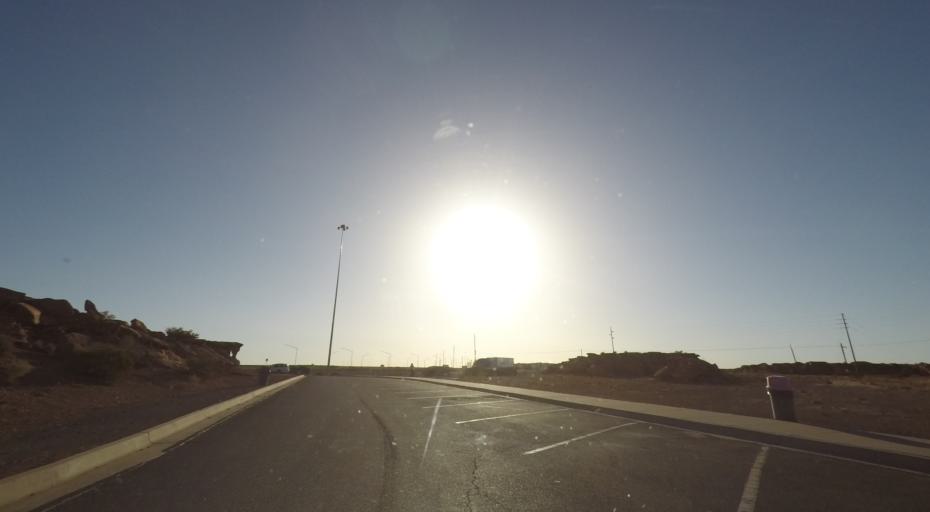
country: US
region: Arizona
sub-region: Coconino County
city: LeChee
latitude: 35.1046
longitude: -110.9926
